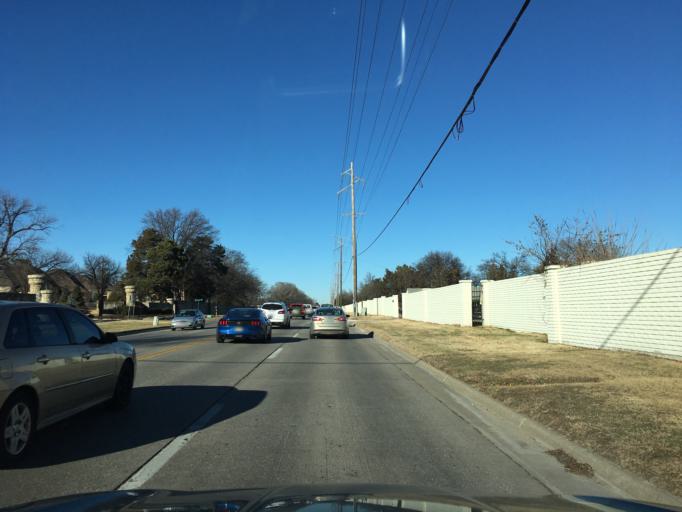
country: US
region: Kansas
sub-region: Sedgwick County
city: Bellaire
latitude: 37.7011
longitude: -97.2446
